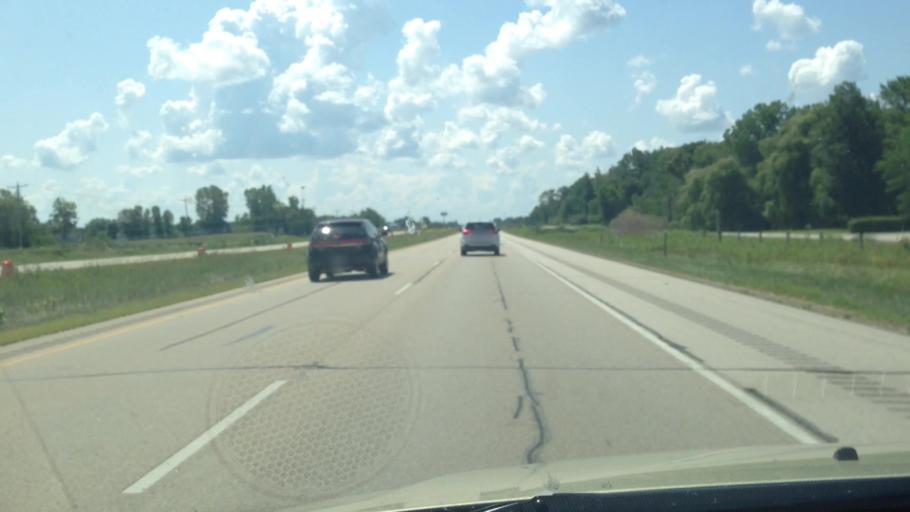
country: US
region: Wisconsin
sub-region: Brown County
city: Suamico
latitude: 44.6948
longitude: -88.0508
